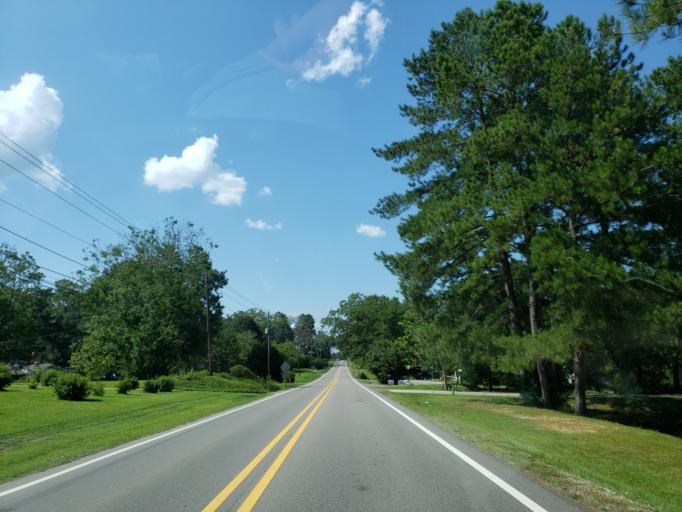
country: US
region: Mississippi
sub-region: Lamar County
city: Sumrall
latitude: 31.4091
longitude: -89.5457
